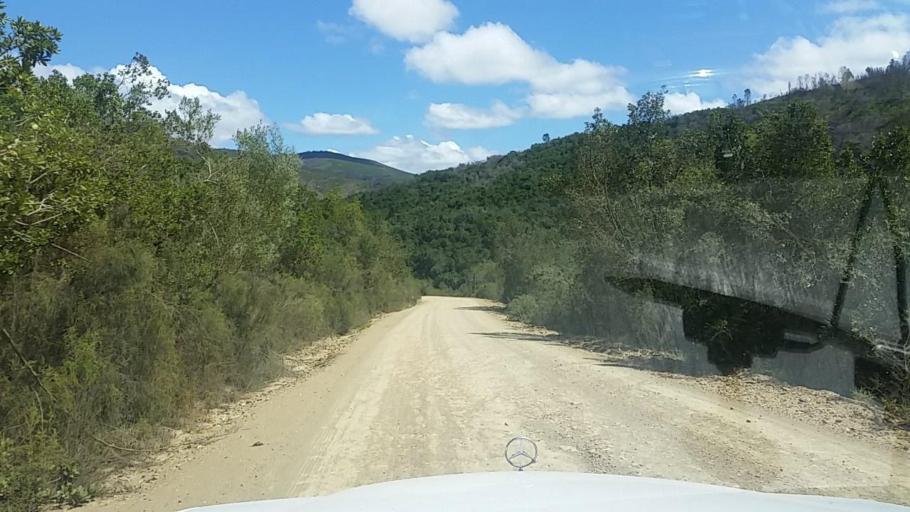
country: ZA
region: Western Cape
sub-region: Eden District Municipality
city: Knysna
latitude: -33.8581
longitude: 23.1813
